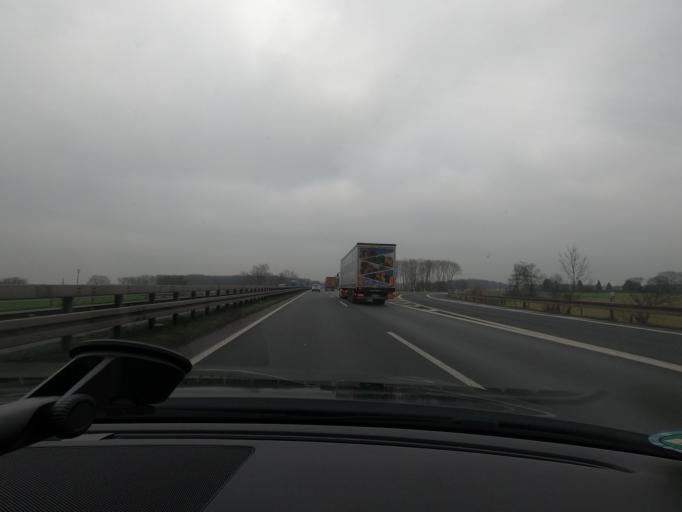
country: DE
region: North Rhine-Westphalia
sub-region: Regierungsbezirk Dusseldorf
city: Viersen
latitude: 51.2332
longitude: 6.3616
